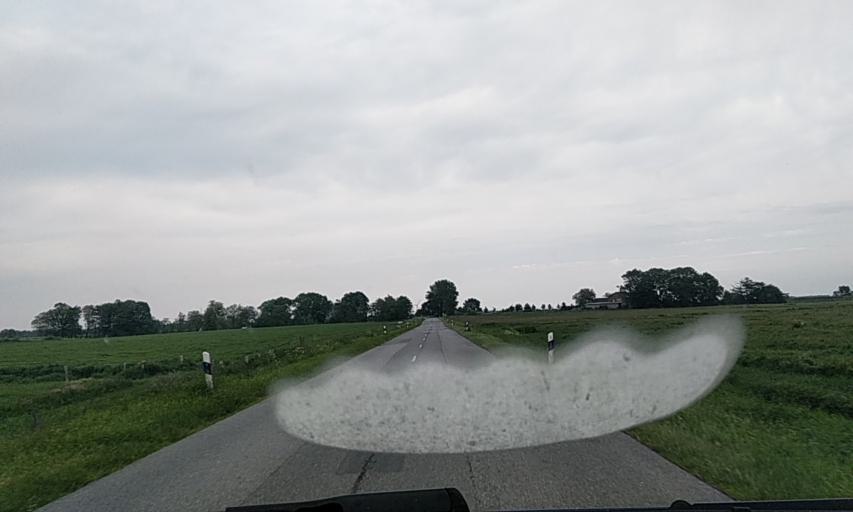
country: DE
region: Schleswig-Holstein
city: Meggerdorf
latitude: 54.3506
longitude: 9.4094
